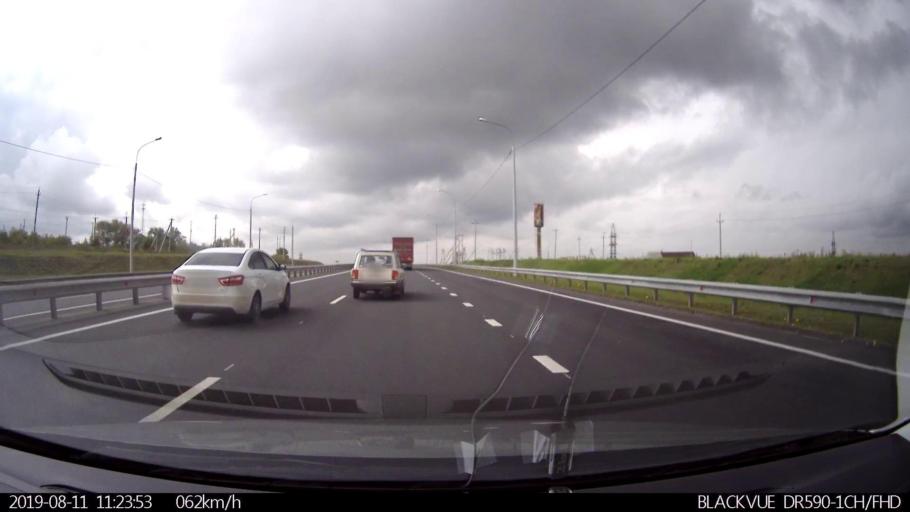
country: RU
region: Ulyanovsk
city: Krasnyy Gulyay
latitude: 54.1321
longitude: 48.2479
